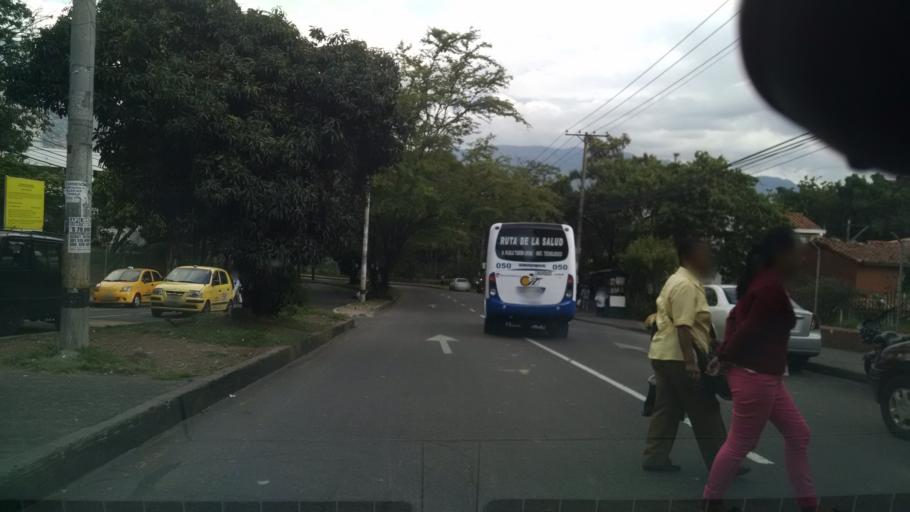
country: CO
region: Antioquia
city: Medellin
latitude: 6.2766
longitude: -75.5808
